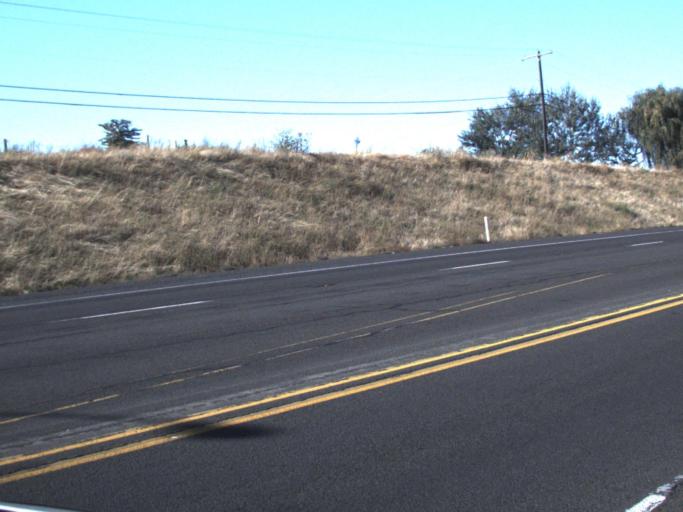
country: US
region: Washington
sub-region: Walla Walla County
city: College Place
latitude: 46.0249
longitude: -118.3888
